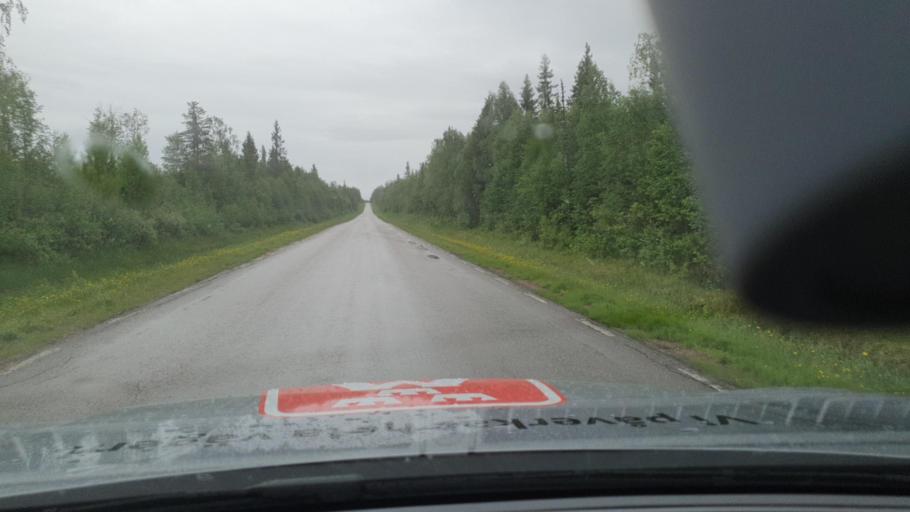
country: SE
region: Norrbotten
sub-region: Pajala Kommun
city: Pajala
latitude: 66.8357
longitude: 23.0972
